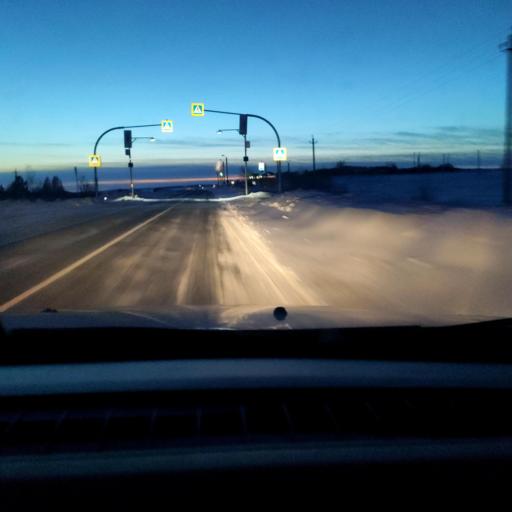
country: RU
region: Samara
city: Kinel'
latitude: 53.2990
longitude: 50.7589
